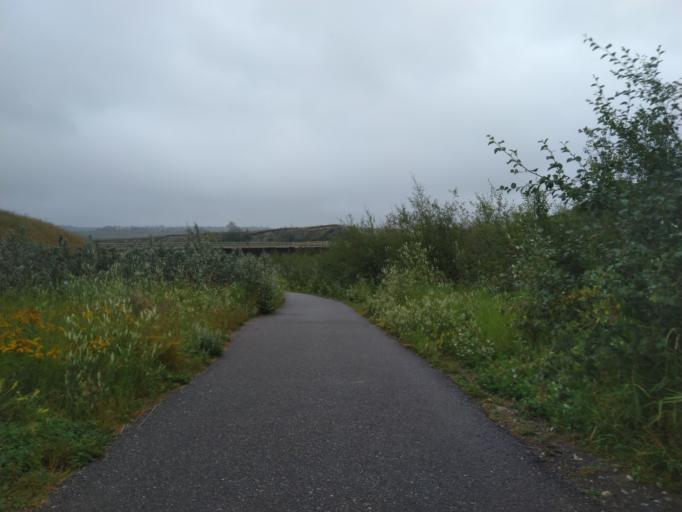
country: CA
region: Alberta
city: Cochrane
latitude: 51.1745
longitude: -114.4477
